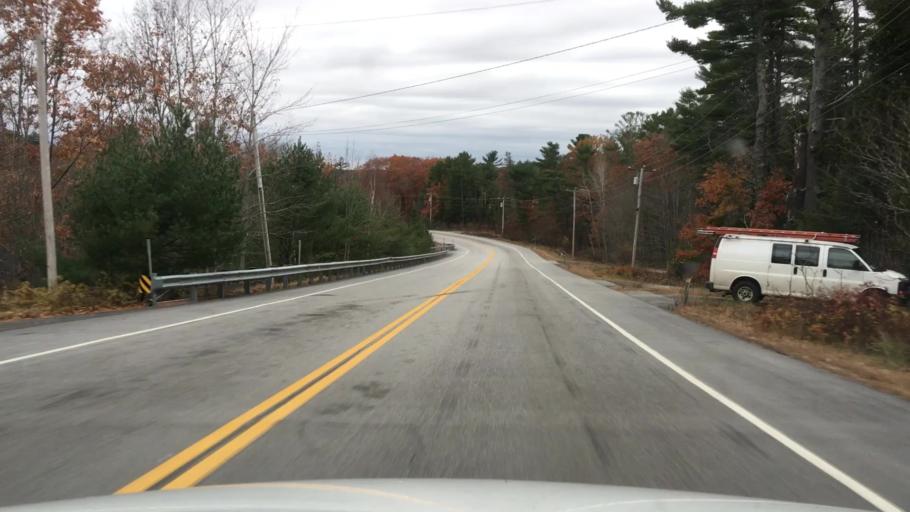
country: US
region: Maine
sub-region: Hancock County
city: Orland
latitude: 44.5563
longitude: -68.6971
